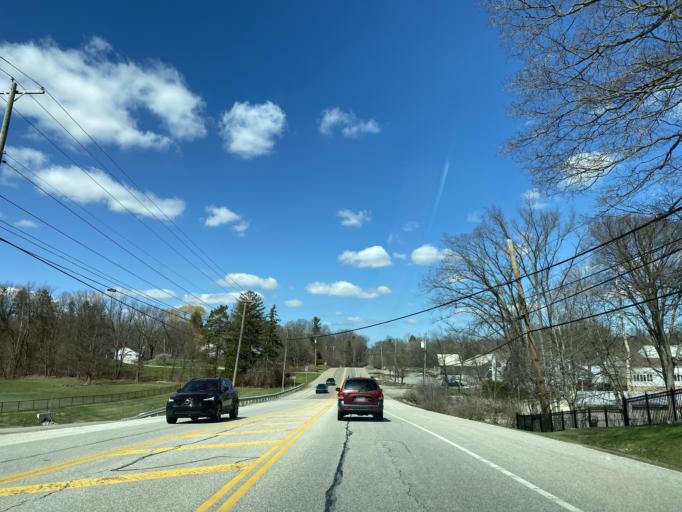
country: US
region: Ohio
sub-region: Summit County
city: Montrose-Ghent
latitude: 41.1695
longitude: -81.6368
